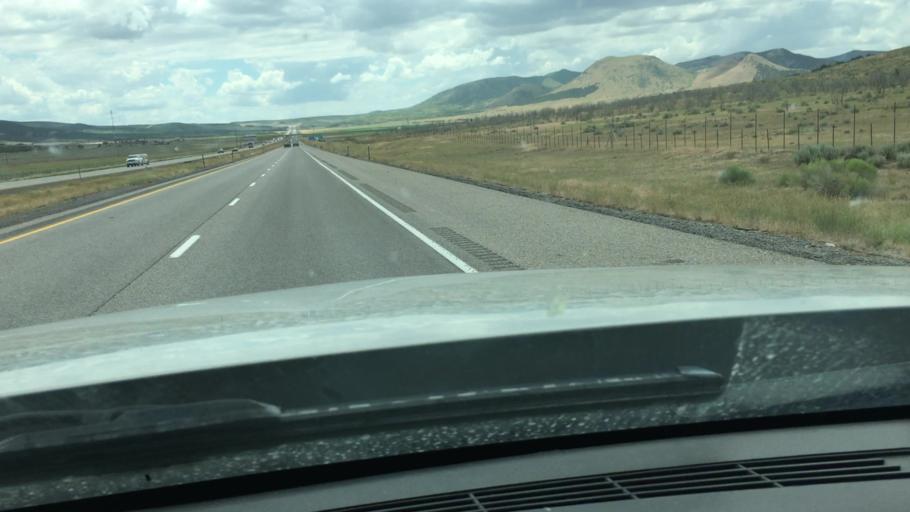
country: US
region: Utah
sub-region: Beaver County
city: Beaver
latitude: 38.5549
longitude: -112.6068
